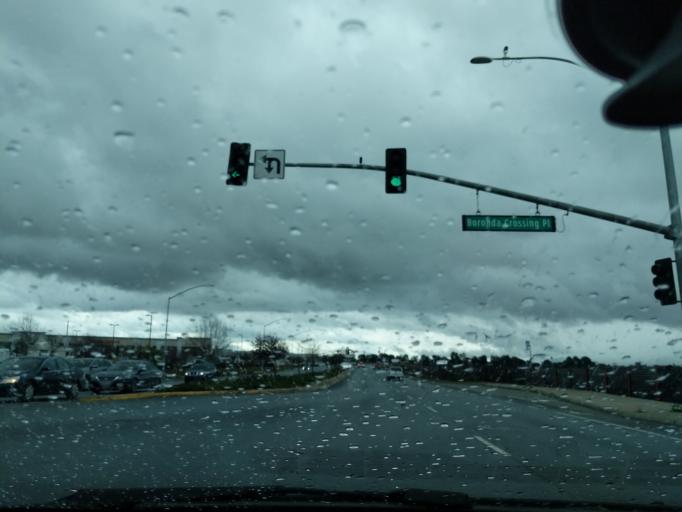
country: US
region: California
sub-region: Monterey County
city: Boronda
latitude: 36.7172
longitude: -121.6669
